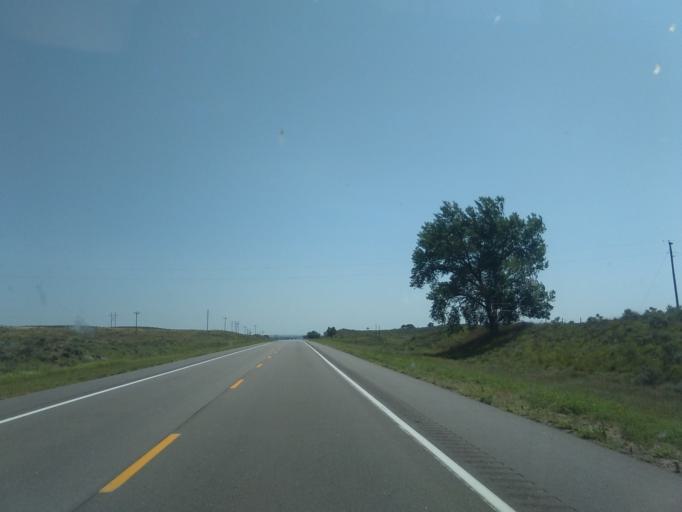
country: US
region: Nebraska
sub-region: Dundy County
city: Benkelman
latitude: 40.0750
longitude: -101.5052
